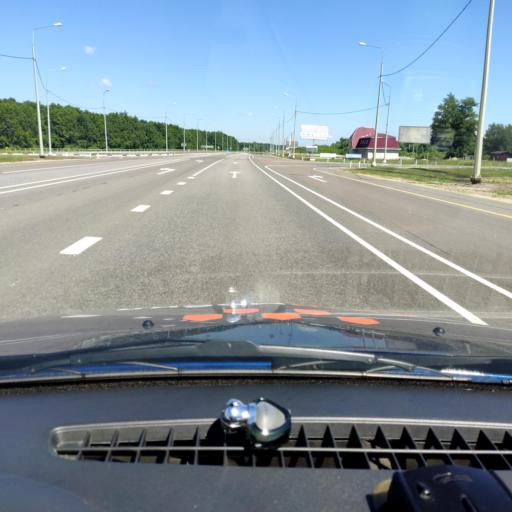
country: RU
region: Orjol
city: Pokrovskoye
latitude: 52.6217
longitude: 36.7728
